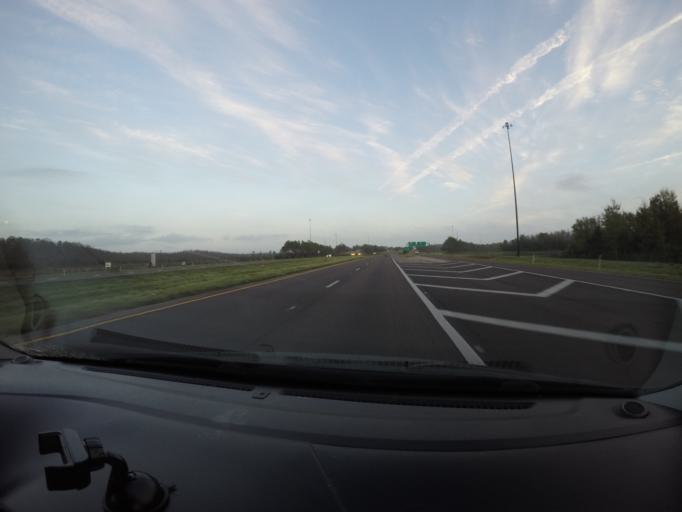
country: US
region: Florida
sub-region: Orange County
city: Conway
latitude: 28.4422
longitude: -81.2299
